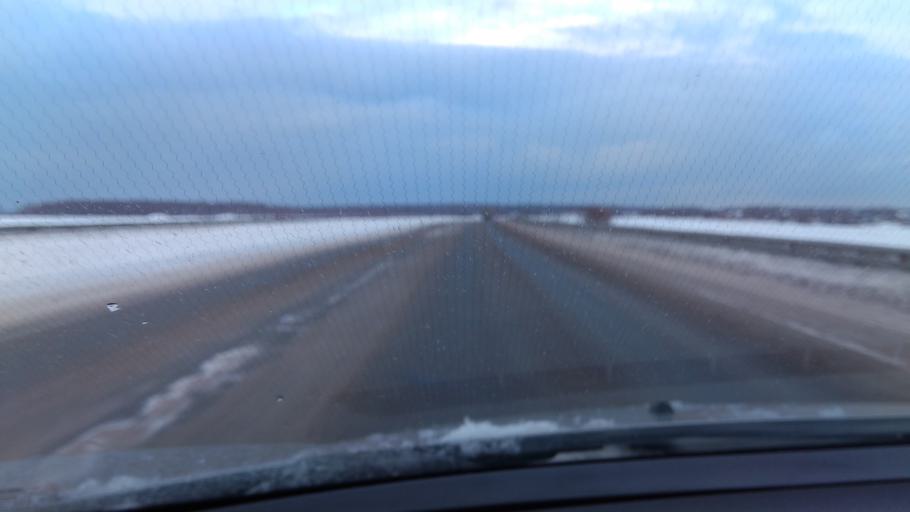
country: RU
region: Sverdlovsk
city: Nev'yansk
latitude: 57.5067
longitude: 60.1739
